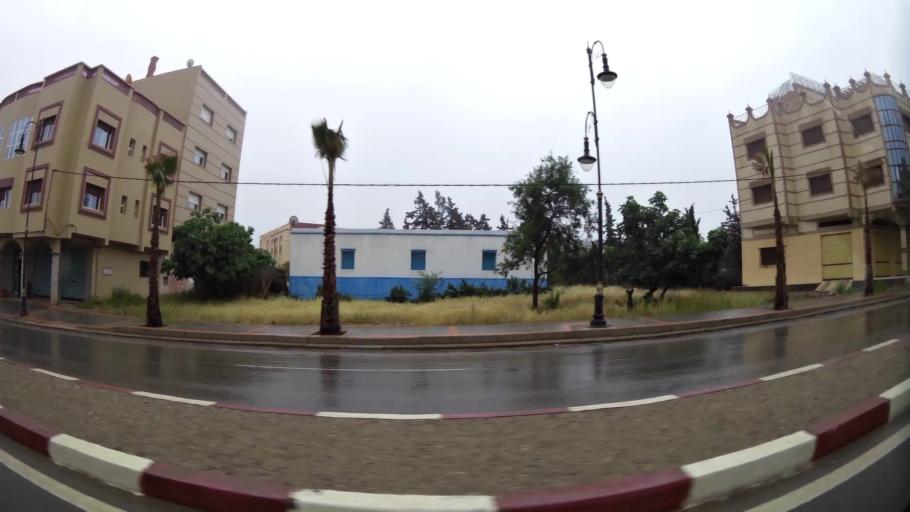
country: MA
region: Taza-Al Hoceima-Taounate
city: Tirhanimine
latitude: 35.1944
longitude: -3.9074
